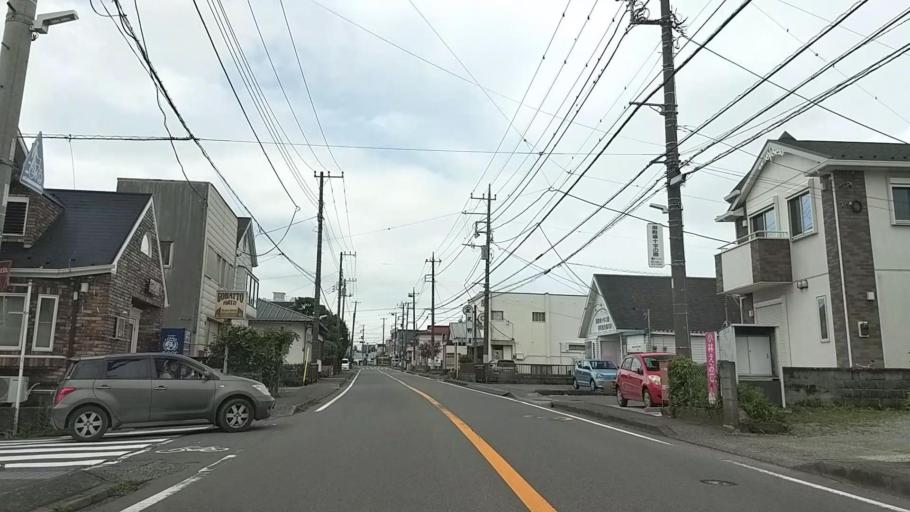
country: JP
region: Shizuoka
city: Gotemba
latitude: 35.3153
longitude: 138.9413
